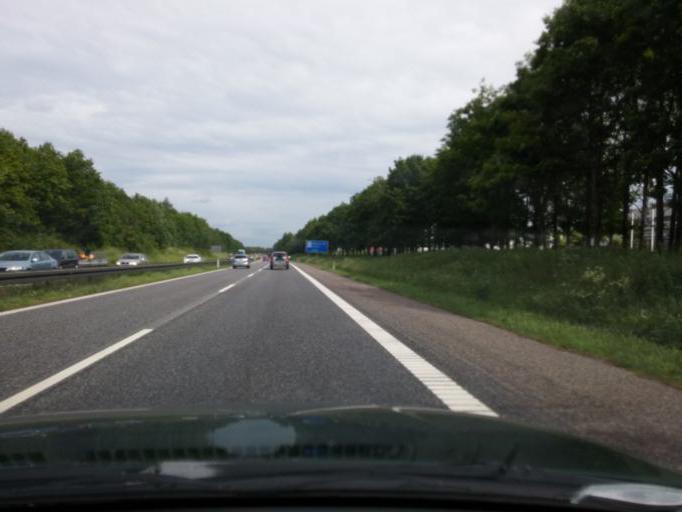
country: DK
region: South Denmark
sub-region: Odense Kommune
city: Bellinge
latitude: 55.3636
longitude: 10.3286
